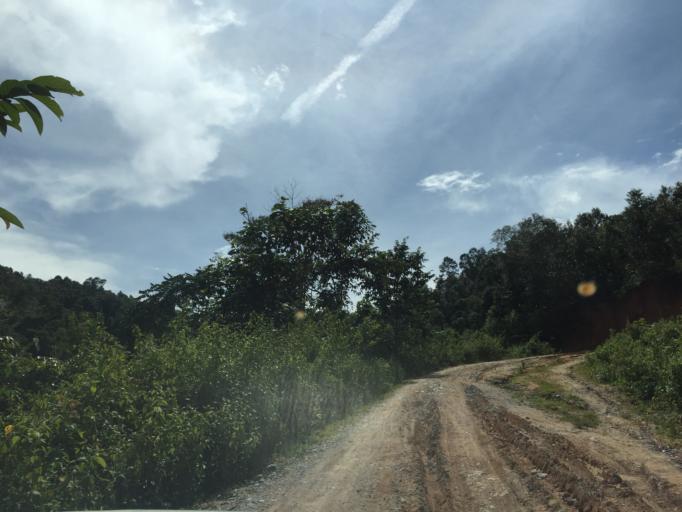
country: LA
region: Xiangkhoang
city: Muang Phonsavan
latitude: 19.3368
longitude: 103.5153
